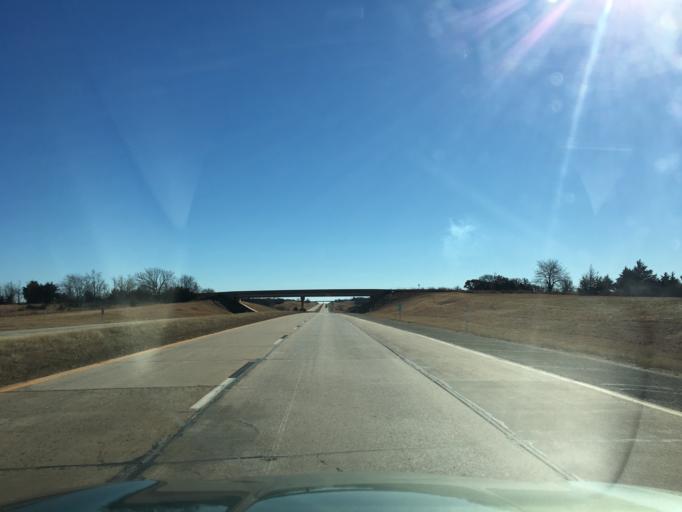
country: US
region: Oklahoma
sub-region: Pawnee County
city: Pawnee
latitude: 36.2919
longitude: -96.9847
